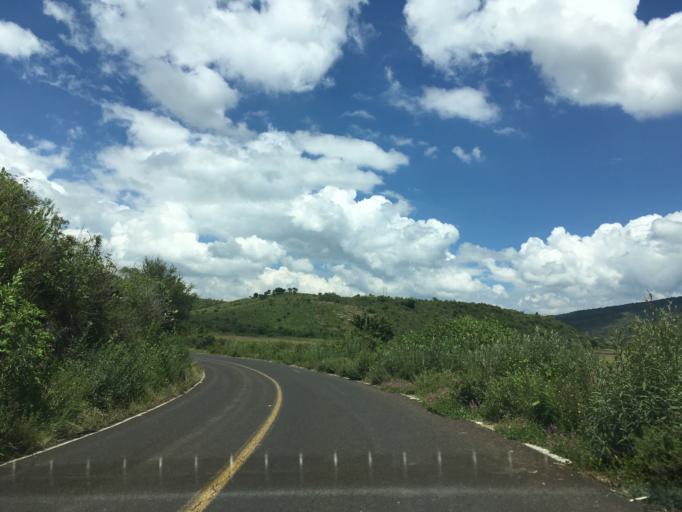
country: MX
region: Michoacan
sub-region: Morelia
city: Cuto de la Esperanza
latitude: 19.7896
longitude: -101.4436
